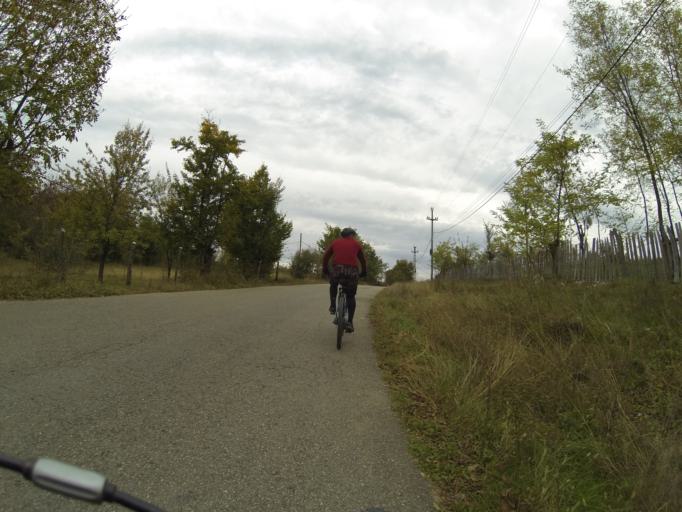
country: RO
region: Gorj
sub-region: Comuna Tismana
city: Sohodol
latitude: 45.0442
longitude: 22.8967
